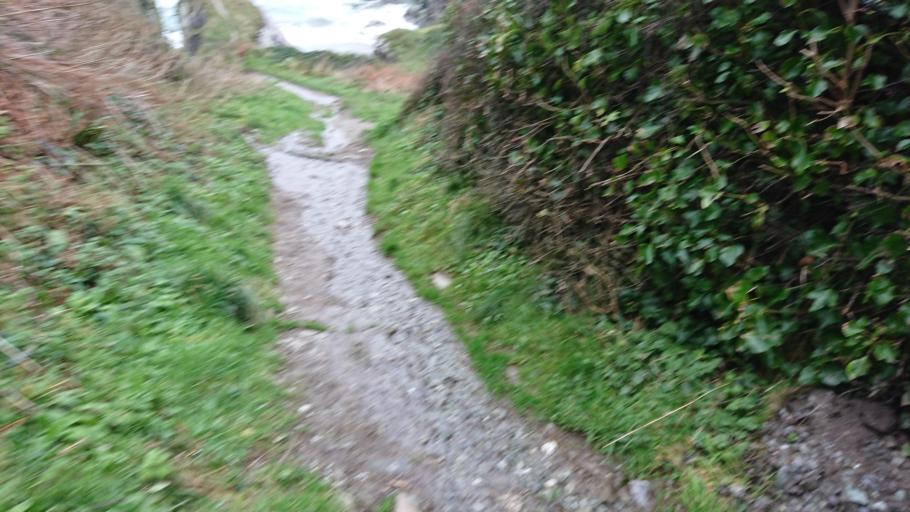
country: GB
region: England
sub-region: Cornwall
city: Fowey
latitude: 50.3330
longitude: -4.5777
